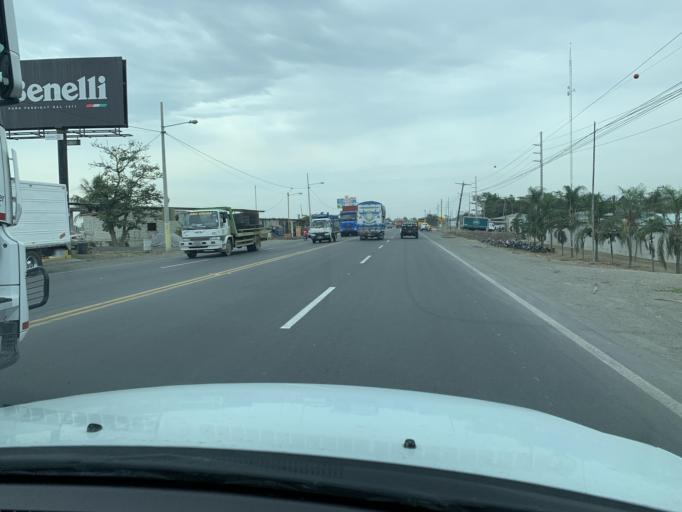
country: EC
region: Guayas
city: Yaguachi Nuevo
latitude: -2.2435
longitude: -79.6369
